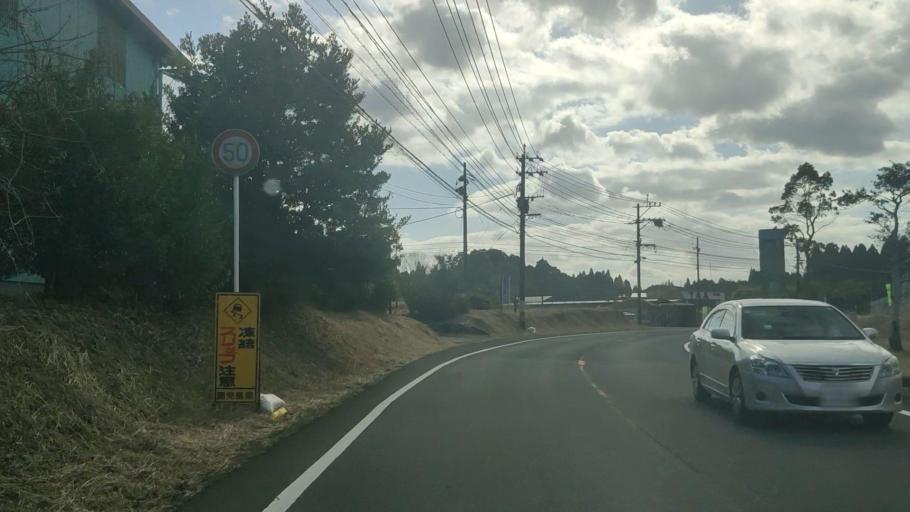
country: JP
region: Kagoshima
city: Okuchi-shinohara
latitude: 31.9254
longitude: 130.7012
